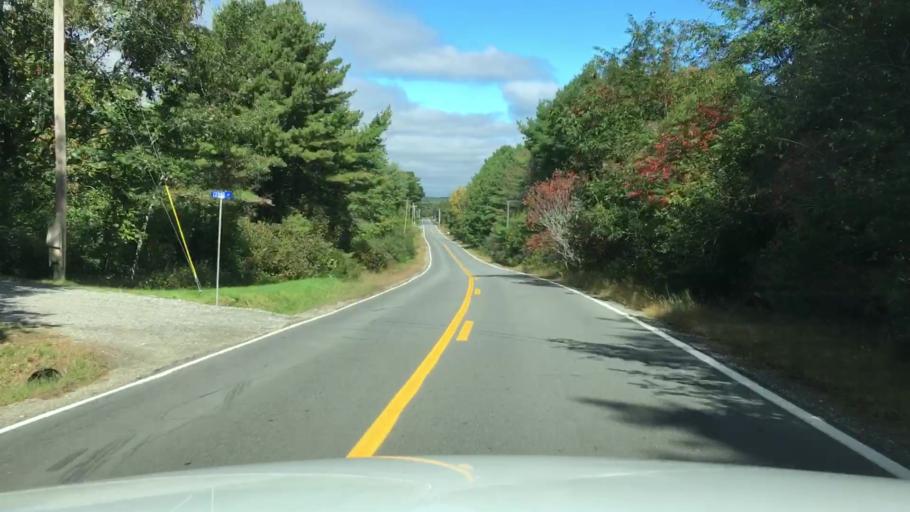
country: US
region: Maine
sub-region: Sagadahoc County
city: North Bath
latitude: 43.9929
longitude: -69.8900
